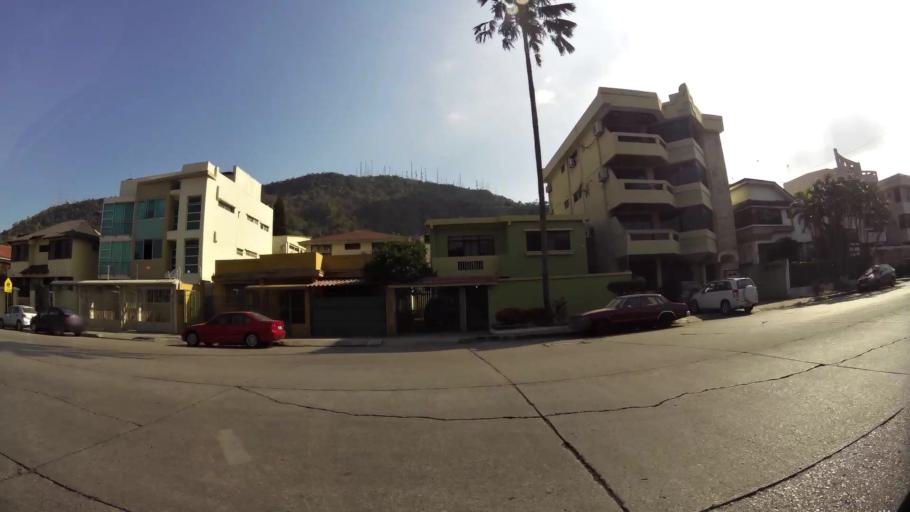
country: EC
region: Guayas
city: Santa Lucia
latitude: -2.1609
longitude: -79.9469
